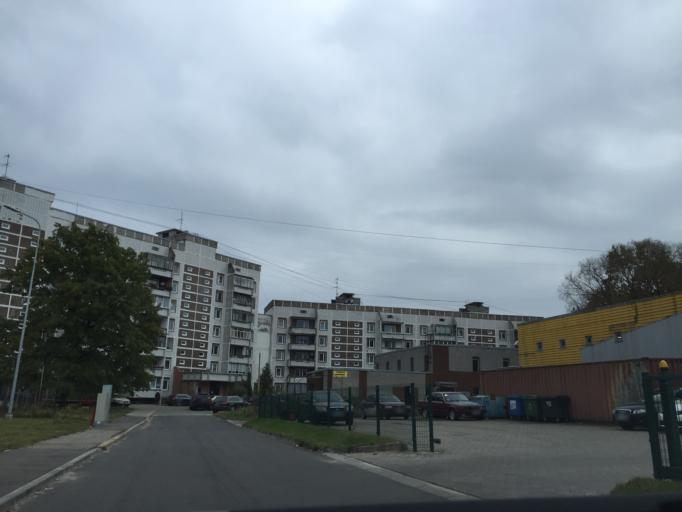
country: LV
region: Riga
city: Riga
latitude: 56.9101
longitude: 24.0960
